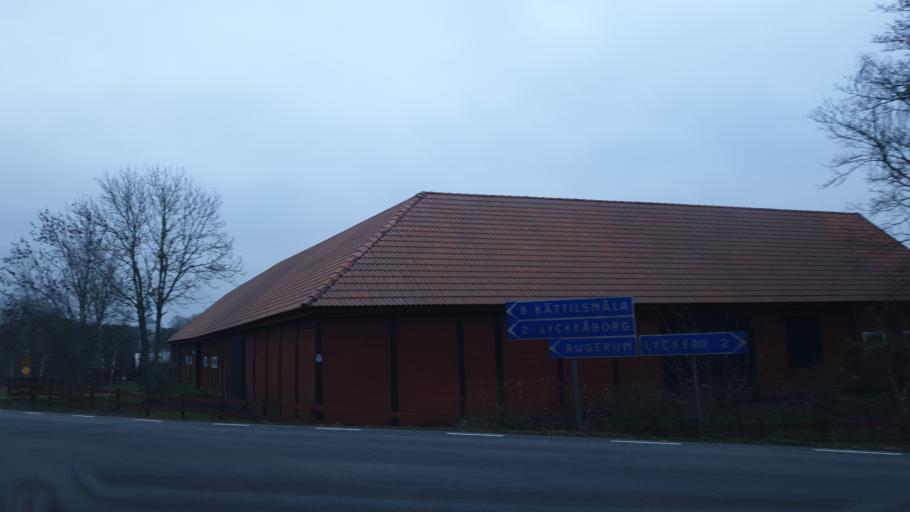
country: SE
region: Blekinge
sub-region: Karlskrona Kommun
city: Rodeby
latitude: 56.2172
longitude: 15.6687
